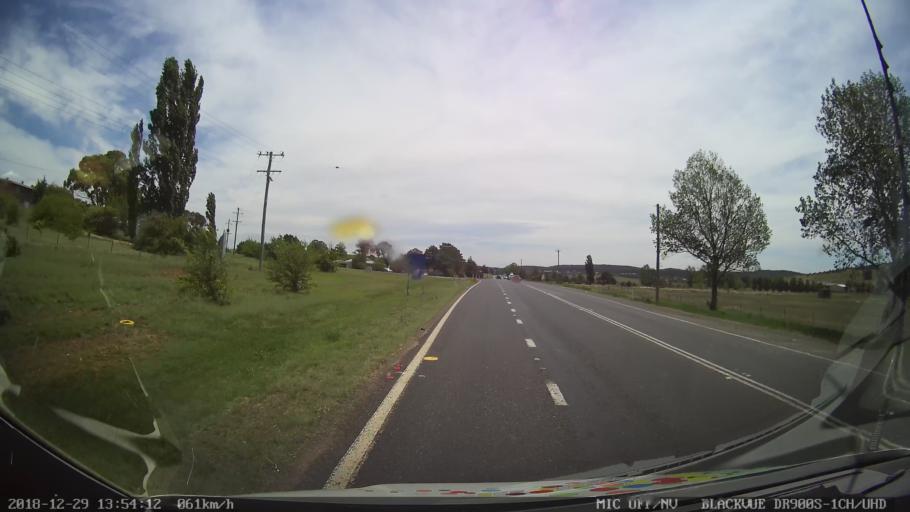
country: AU
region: New South Wales
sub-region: Cooma-Monaro
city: Cooma
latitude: -36.2129
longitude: 149.1530
